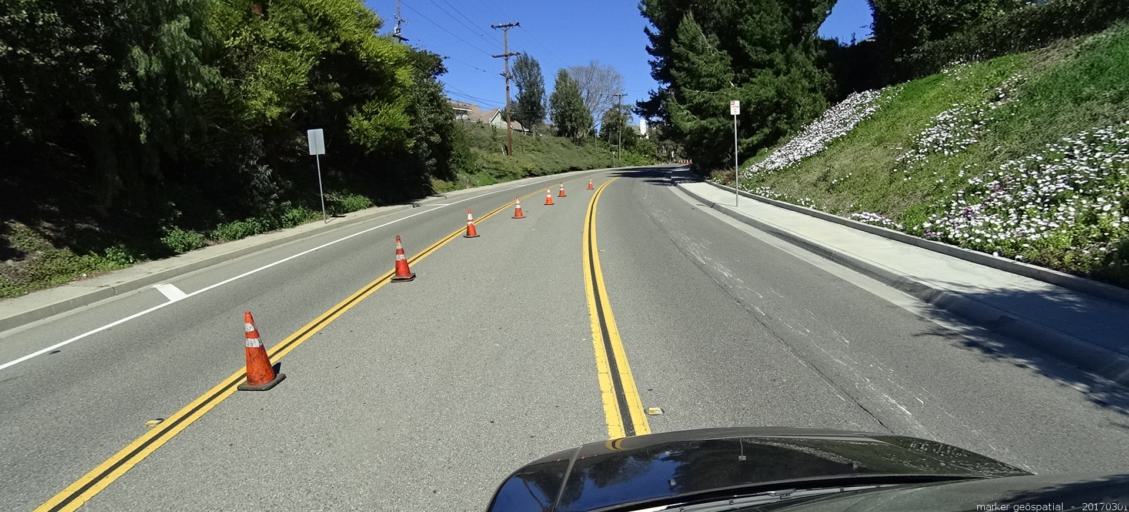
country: US
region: California
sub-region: Orange County
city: Villa Park
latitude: 33.8368
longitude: -117.8309
